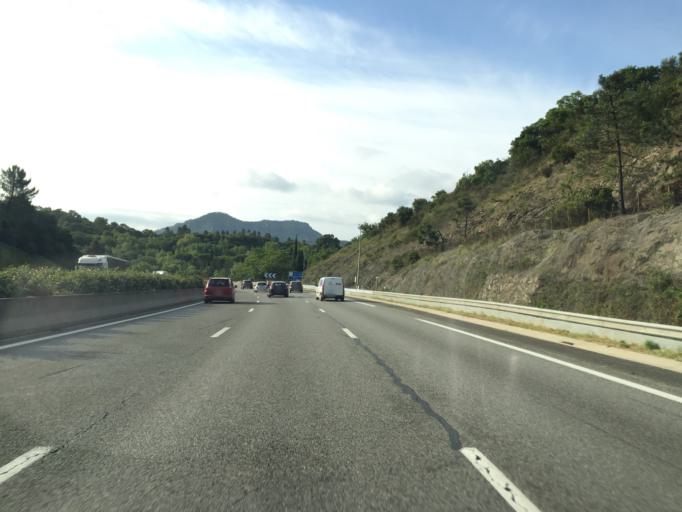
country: FR
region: Provence-Alpes-Cote d'Azur
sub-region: Departement du Var
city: Tanneron
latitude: 43.5432
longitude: 6.8355
